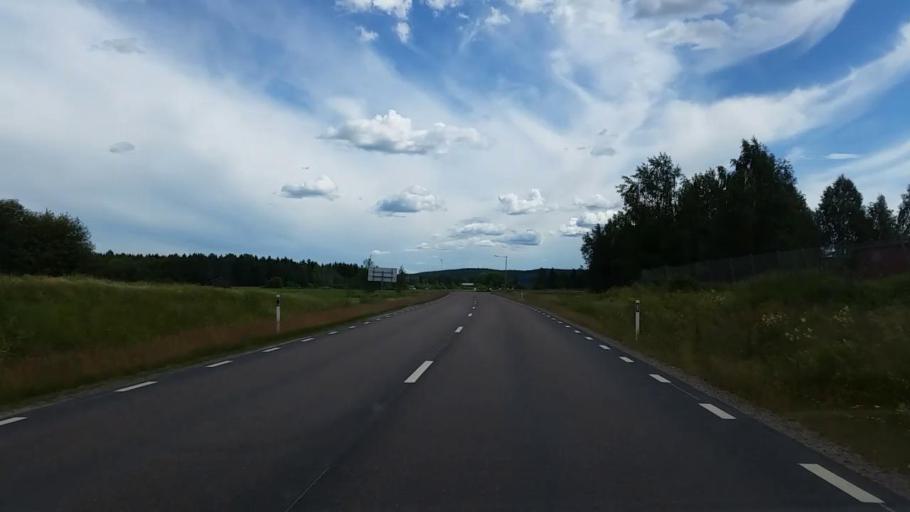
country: SE
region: Gaevleborg
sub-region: Ovanakers Kommun
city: Edsbyn
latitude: 61.3747
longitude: 15.8426
